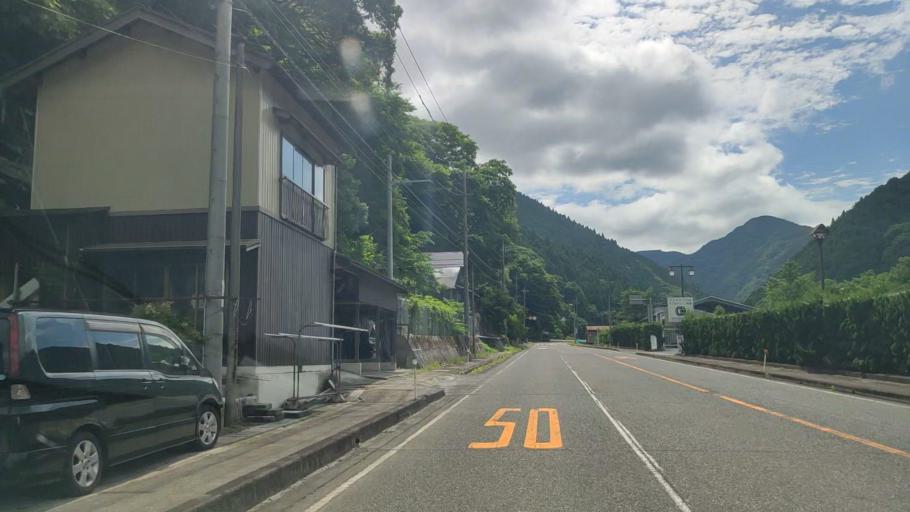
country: JP
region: Okayama
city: Niimi
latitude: 35.2174
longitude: 133.4571
